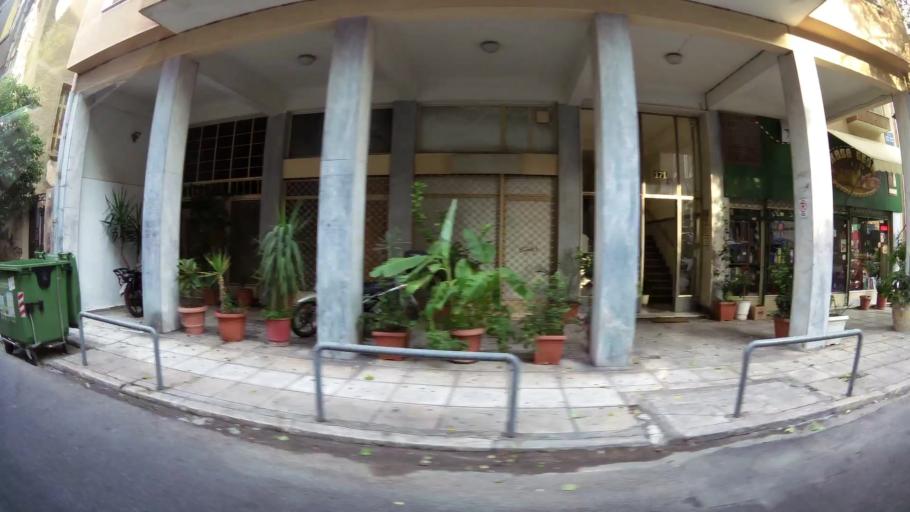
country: GR
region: Attica
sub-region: Nomarchia Athinas
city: Kipseli
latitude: 37.9887
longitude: 23.7445
